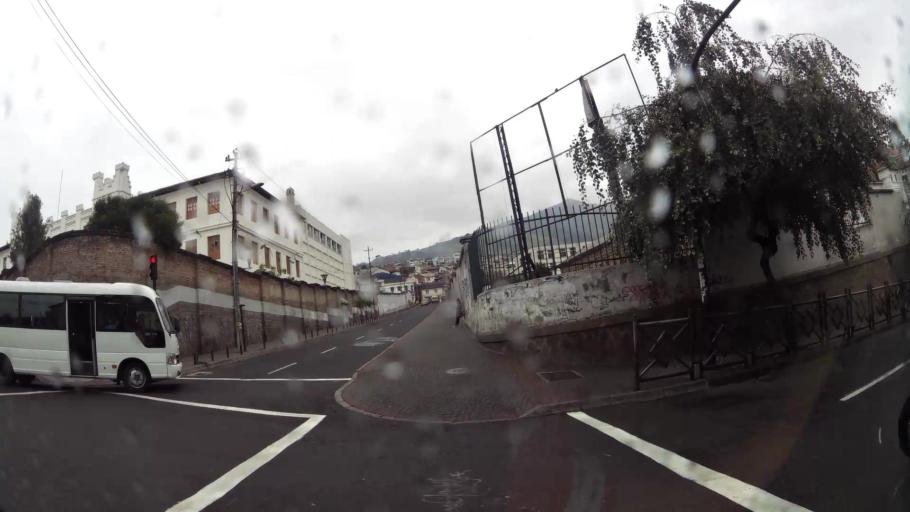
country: EC
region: Pichincha
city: Quito
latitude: -0.2132
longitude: -78.5048
